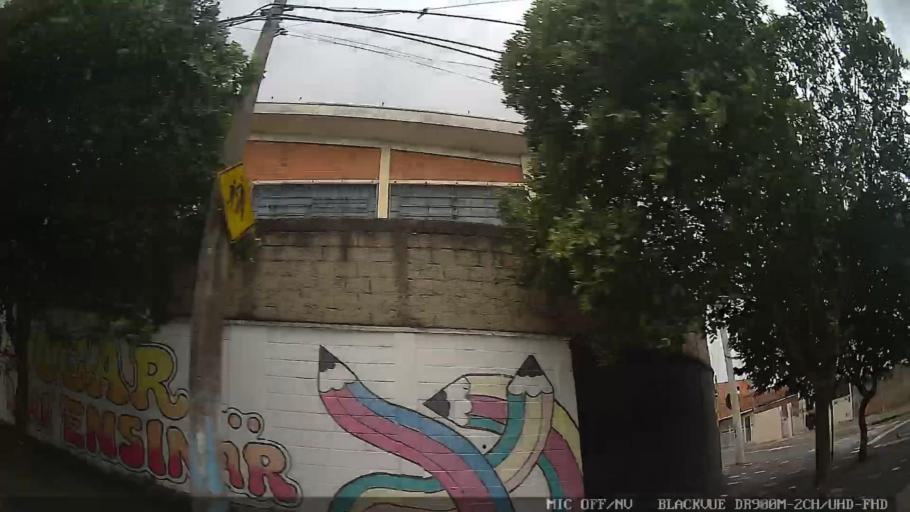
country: BR
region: Sao Paulo
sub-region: Indaiatuba
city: Indaiatuba
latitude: -23.1293
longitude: -47.2412
